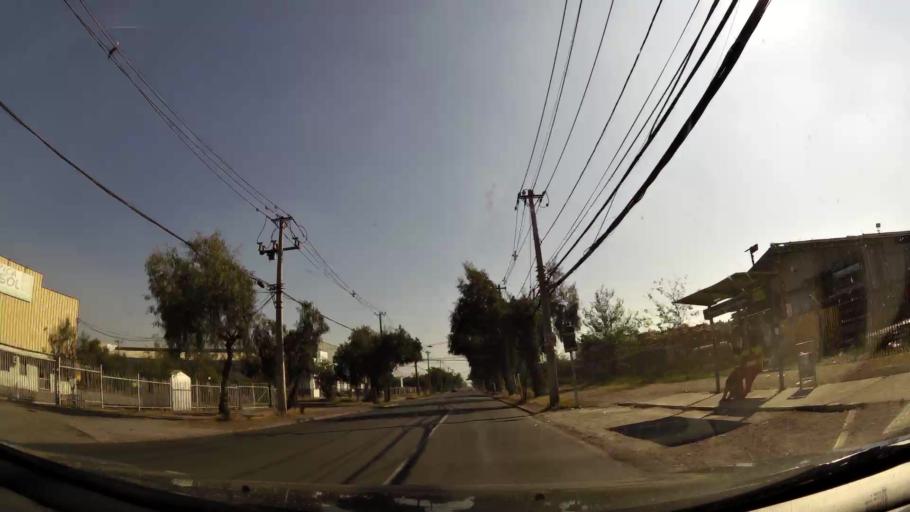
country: CL
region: Santiago Metropolitan
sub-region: Provincia de Chacabuco
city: Chicureo Abajo
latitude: -33.3355
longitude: -70.7193
